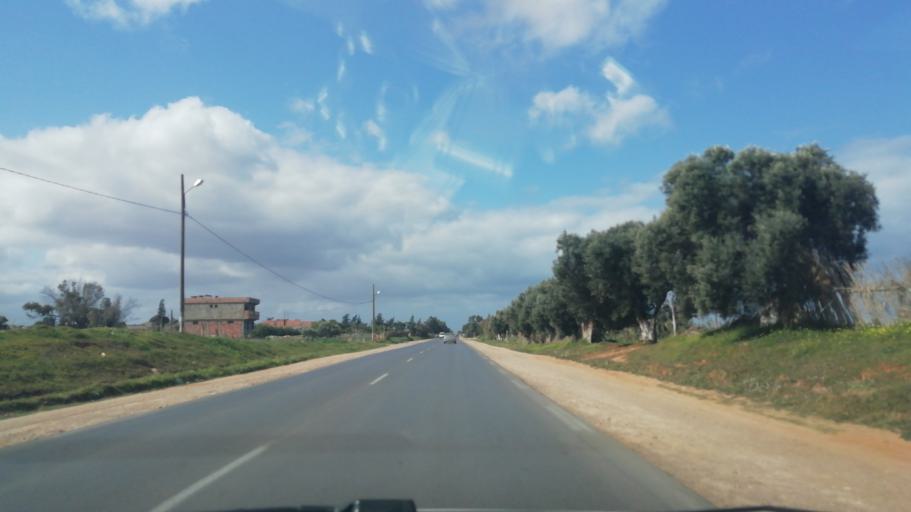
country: DZ
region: Relizane
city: Mazouna
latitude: 36.2576
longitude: 0.5933
